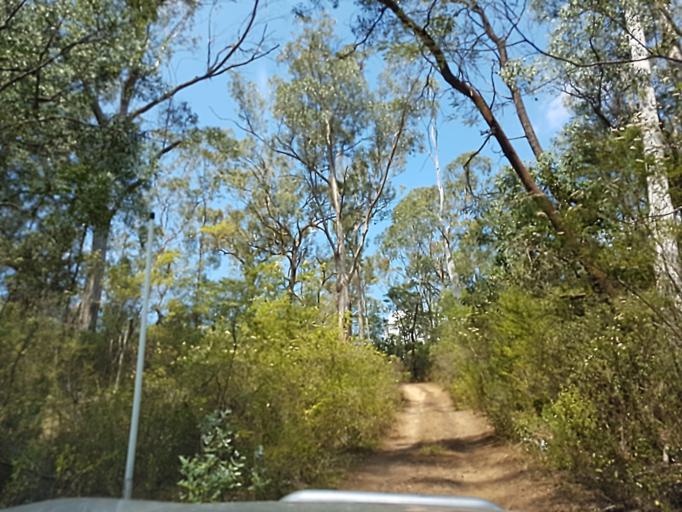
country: AU
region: Victoria
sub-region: East Gippsland
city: Lakes Entrance
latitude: -37.3991
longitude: 148.3214
